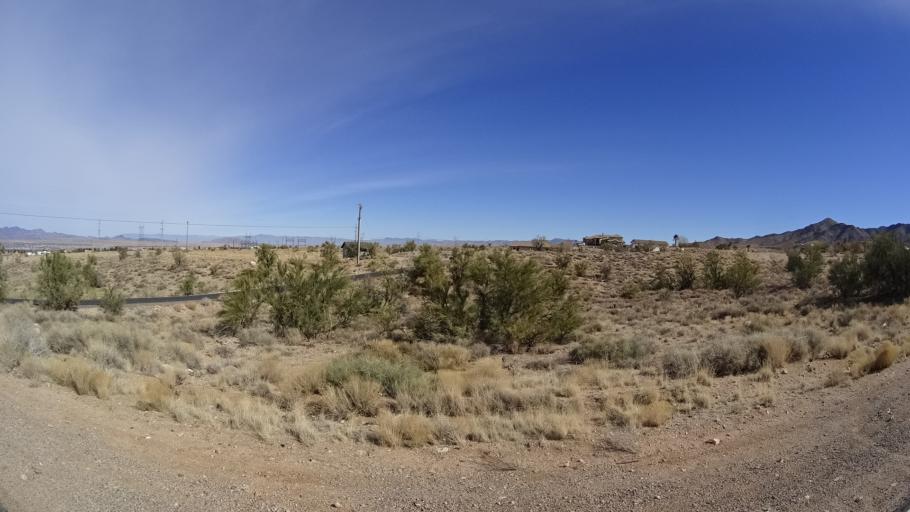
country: US
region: Arizona
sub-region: Mohave County
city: Kingman
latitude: 35.1718
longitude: -113.9823
